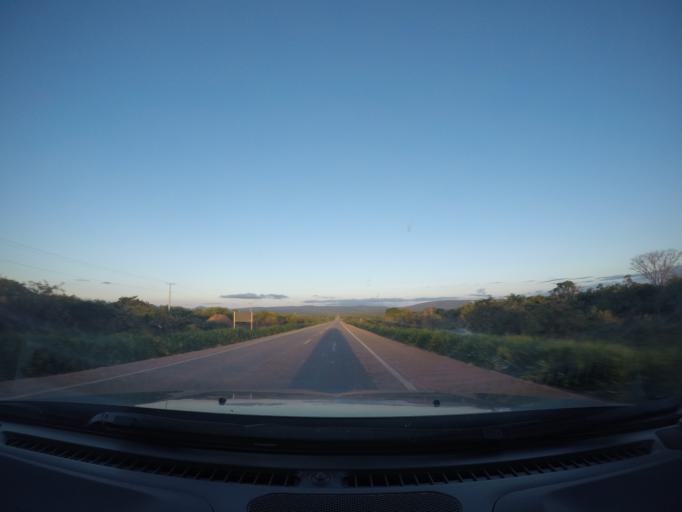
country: BR
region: Bahia
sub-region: Seabra
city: Seabra
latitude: -12.4075
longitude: -41.9618
